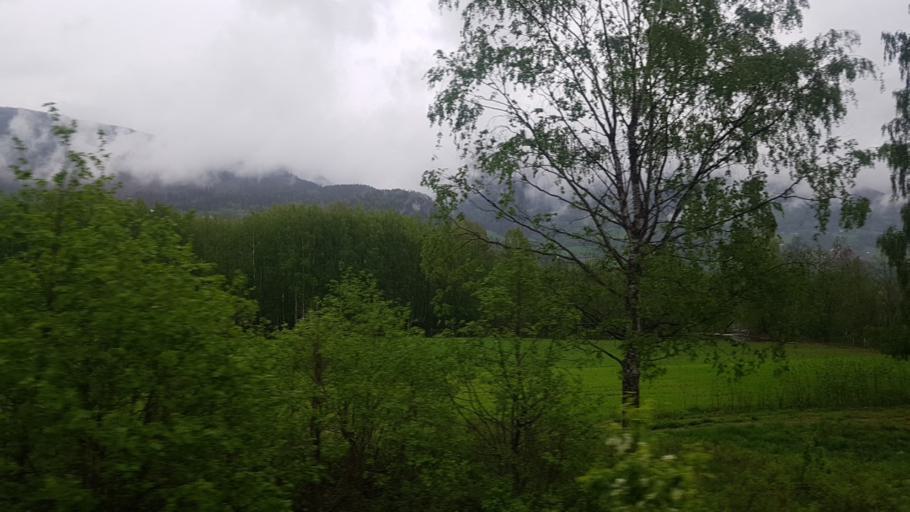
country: NO
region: Oppland
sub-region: Ringebu
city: Ringebu
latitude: 61.4606
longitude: 10.1924
